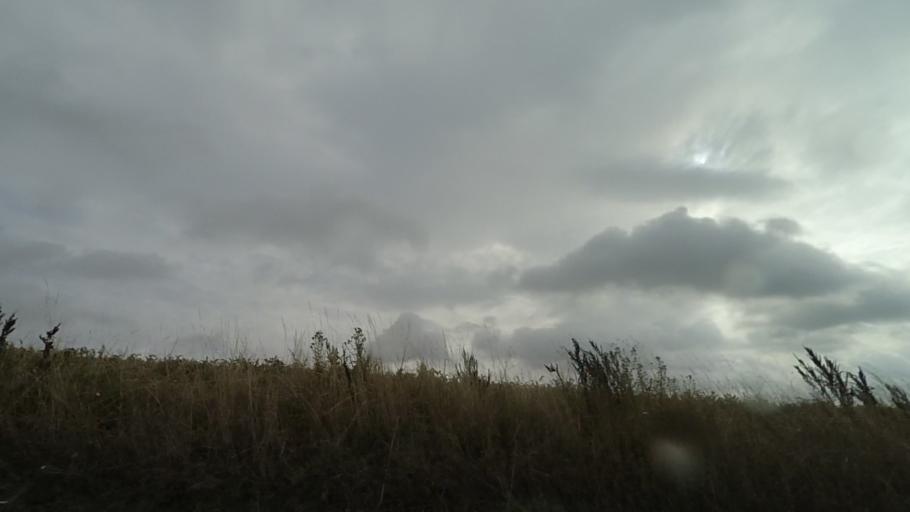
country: DK
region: Central Jutland
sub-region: Syddjurs Kommune
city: Ronde
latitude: 56.3027
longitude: 10.4435
